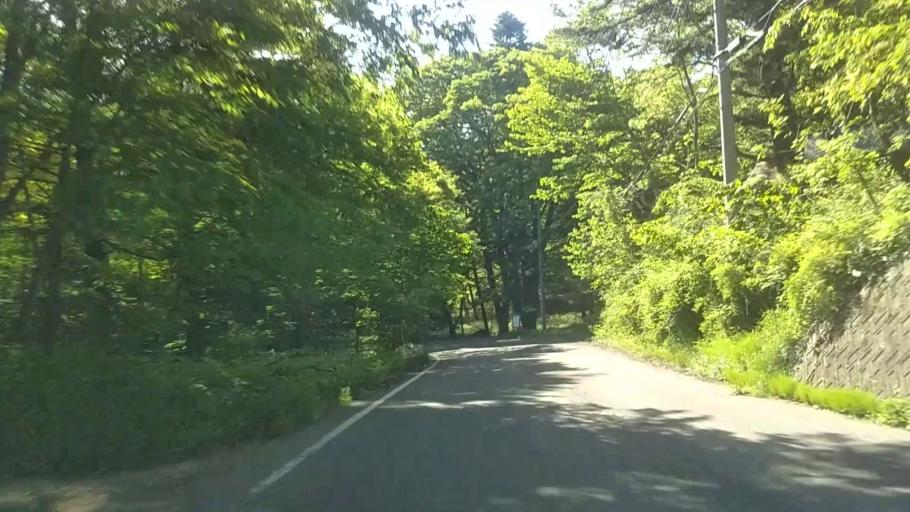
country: JP
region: Yamanashi
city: Nirasaki
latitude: 35.8820
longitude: 138.3678
